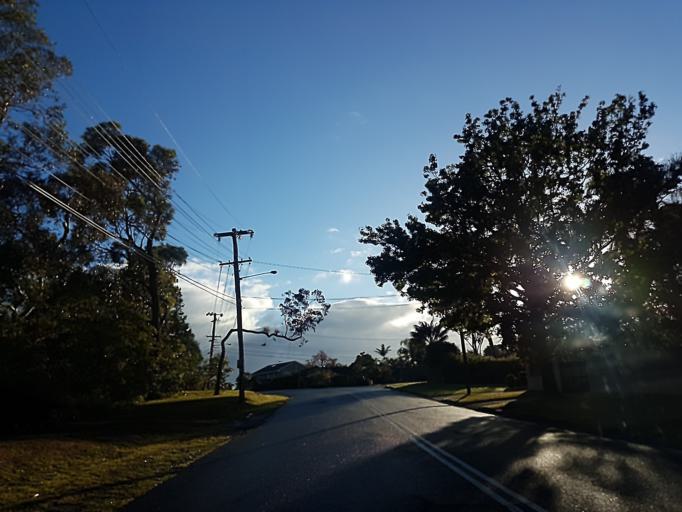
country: AU
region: New South Wales
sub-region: Warringah
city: Davidson
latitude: -33.7390
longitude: 151.2048
